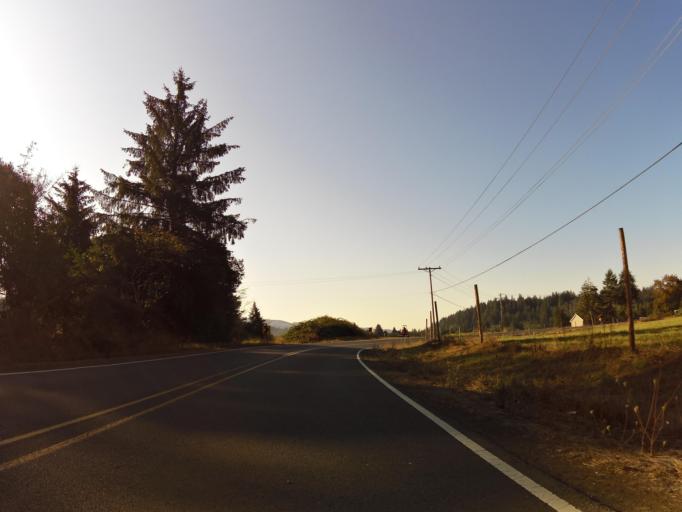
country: US
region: Oregon
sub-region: Tillamook County
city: Tillamook
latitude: 45.4279
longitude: -123.7777
